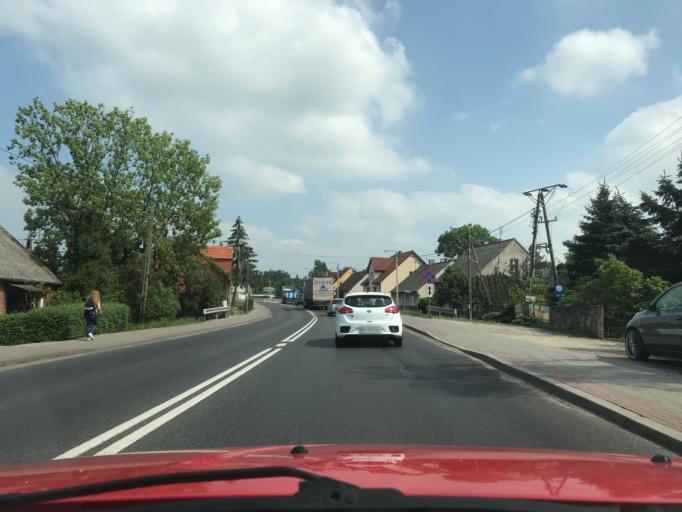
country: PL
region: Greater Poland Voivodeship
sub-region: Powiat jarocinski
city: Kotlin
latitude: 51.9188
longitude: 17.6490
